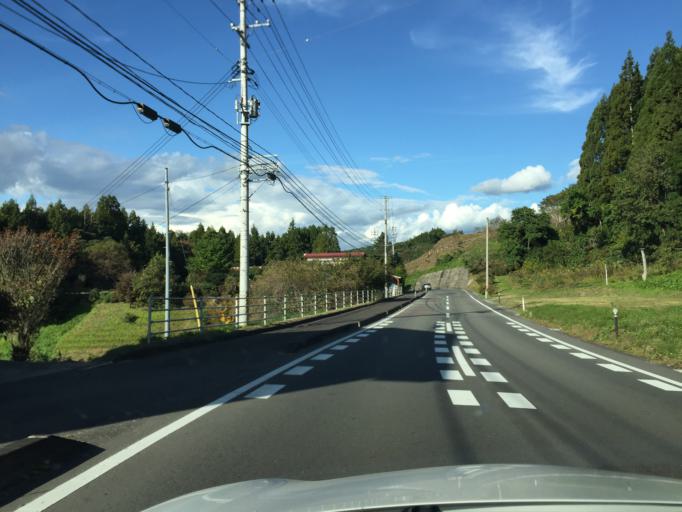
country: JP
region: Fukushima
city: Ishikawa
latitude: 37.2053
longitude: 140.4537
